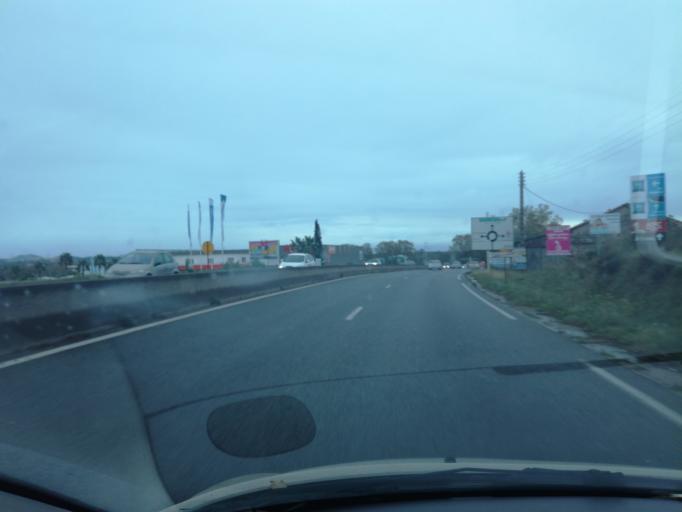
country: FR
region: Provence-Alpes-Cote d'Azur
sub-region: Departement du Var
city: Puget-sur-Argens
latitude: 43.4415
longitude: 6.7051
